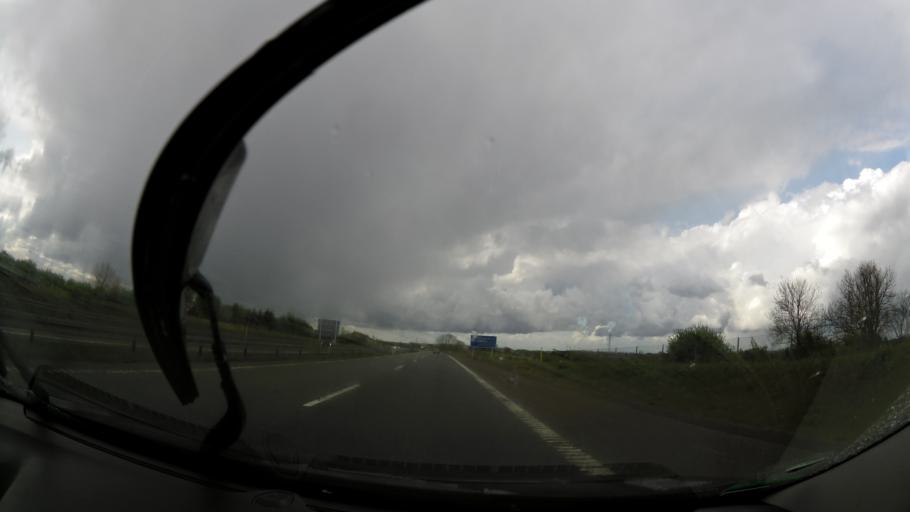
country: DK
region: South Denmark
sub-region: Svendborg Kommune
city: Svendborg
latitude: 55.0818
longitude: 10.5735
